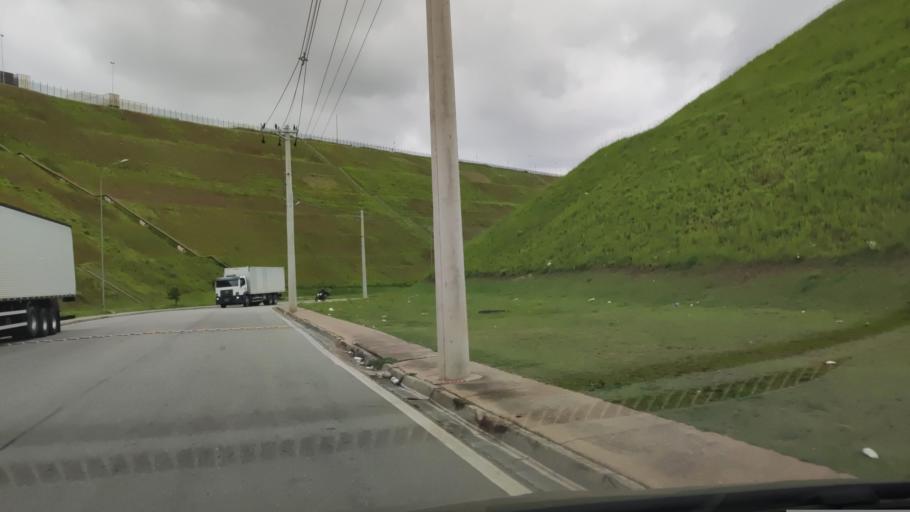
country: BR
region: Sao Paulo
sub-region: Cajamar
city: Cajamar
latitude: -23.3328
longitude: -46.8475
